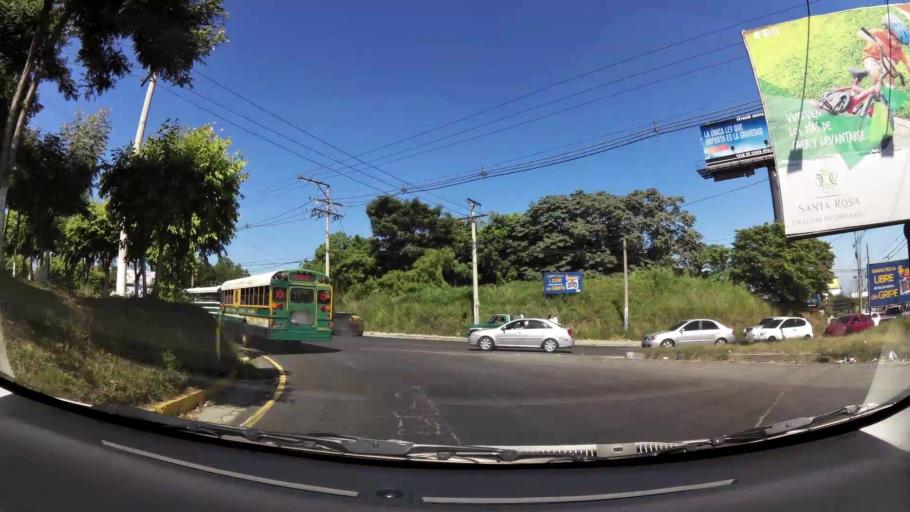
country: SV
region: La Libertad
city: Santa Tecla
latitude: 13.6631
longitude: -89.2777
